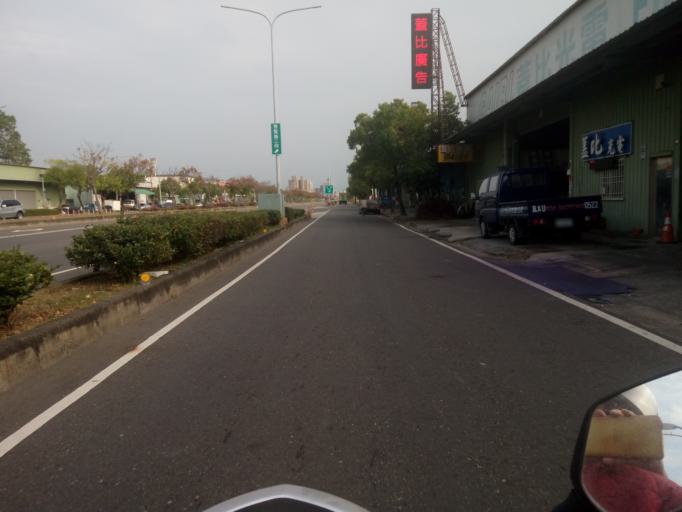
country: TW
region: Taiwan
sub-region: Chiayi
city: Jiayi Shi
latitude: 23.4834
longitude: 120.4151
